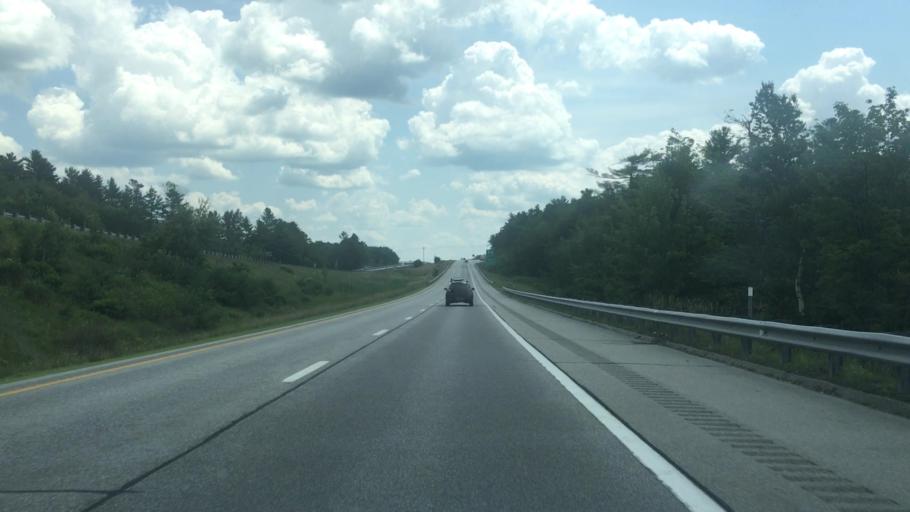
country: US
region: New Hampshire
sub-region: Merrimack County
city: New London
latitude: 43.4314
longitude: -72.0415
